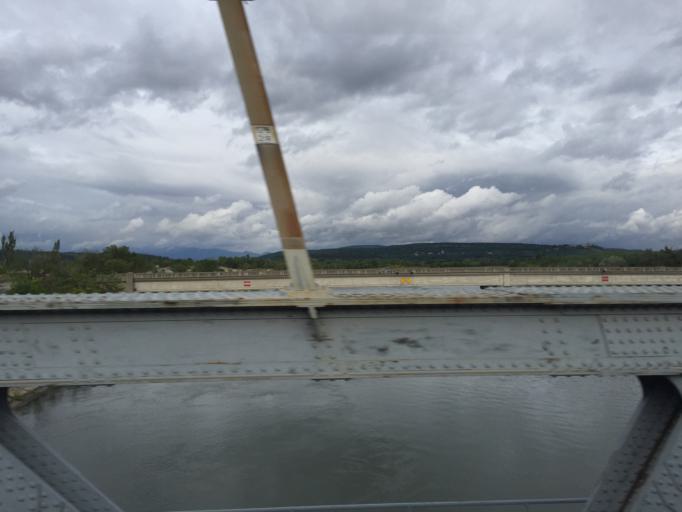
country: FR
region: Rhone-Alpes
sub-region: Departement de la Drome
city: Donzere
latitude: 44.4127
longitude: 4.7094
